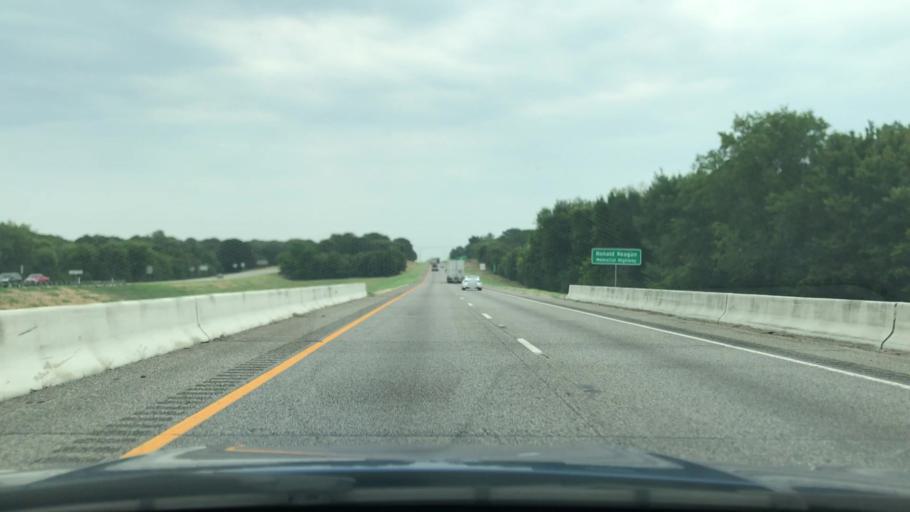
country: US
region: Texas
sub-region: Van Zandt County
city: Canton
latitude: 32.5752
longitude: -95.8475
